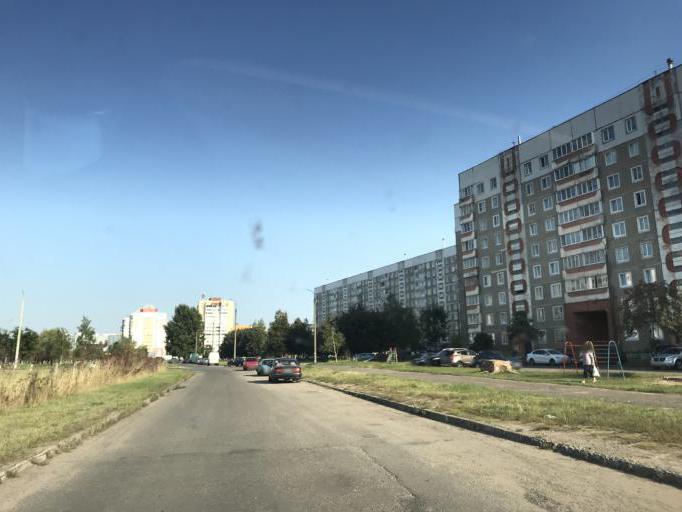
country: BY
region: Mogilev
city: Mahilyow
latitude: 53.8791
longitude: 30.3619
